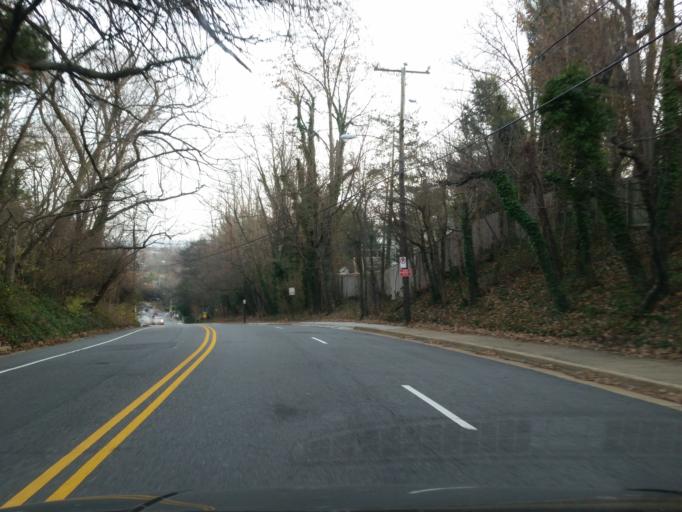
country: US
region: Virginia
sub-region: City of Alexandria
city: Alexandria
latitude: 38.8192
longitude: -77.0687
